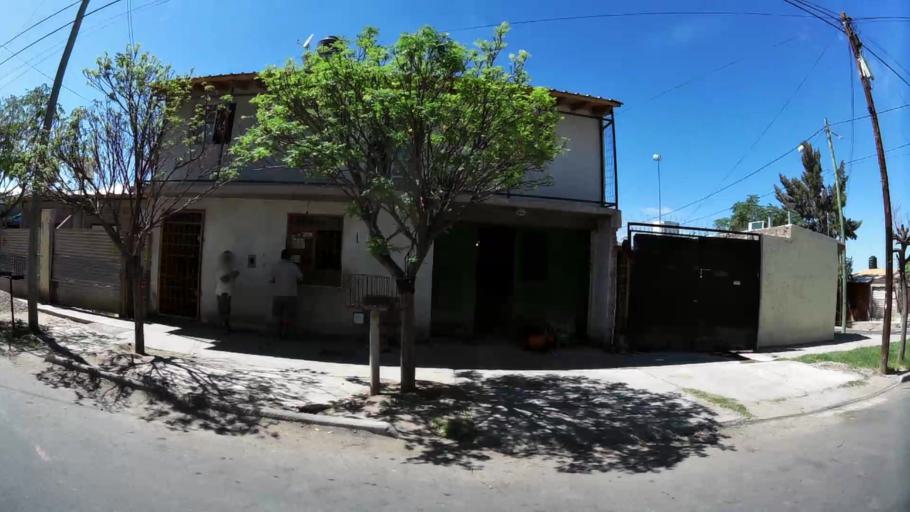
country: AR
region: Mendoza
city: Las Heras
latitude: -32.8500
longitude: -68.8713
